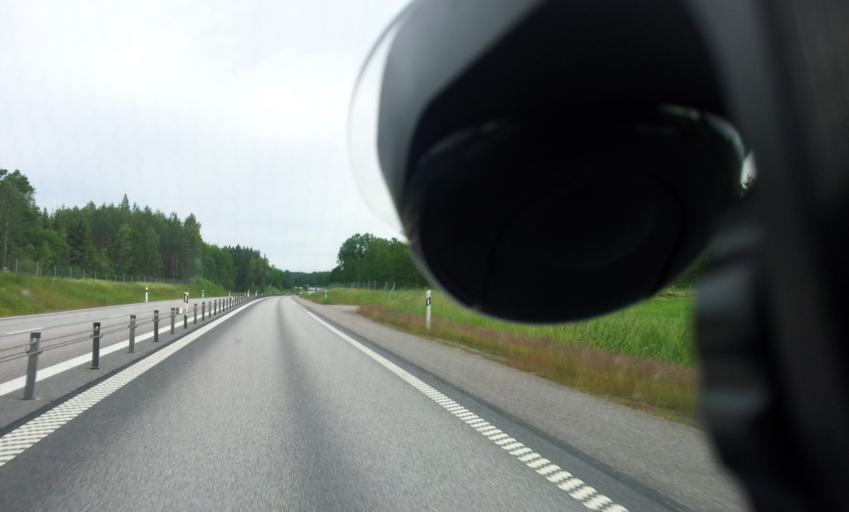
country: SE
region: OEstergoetland
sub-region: Valdemarsviks Kommun
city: Gusum
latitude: 58.3688
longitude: 16.4291
